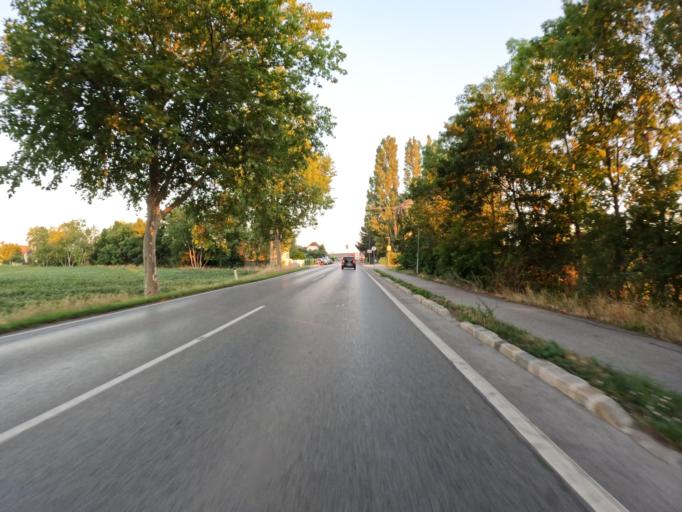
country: AT
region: Lower Austria
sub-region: Politischer Bezirk Baden
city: Pfaffstatten
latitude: 47.9933
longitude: 16.2753
